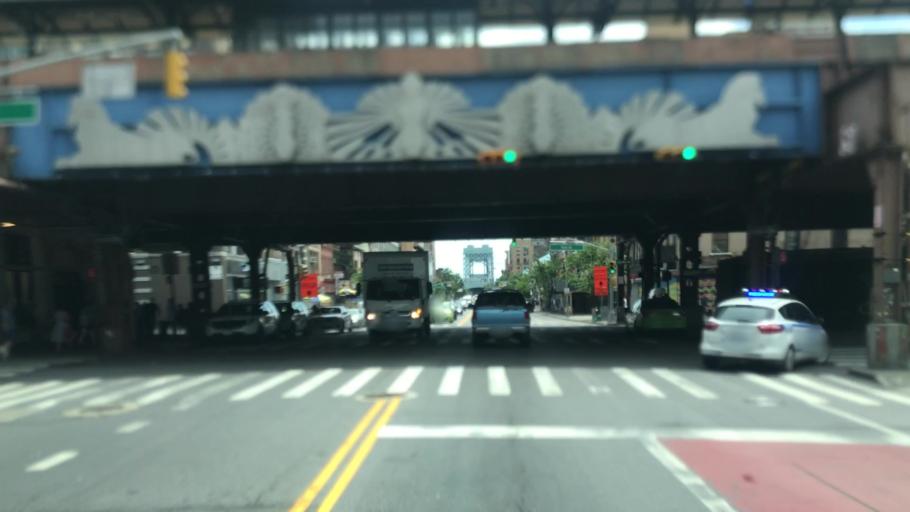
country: US
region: New York
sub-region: New York County
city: Manhattan
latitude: 40.8052
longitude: -73.9393
